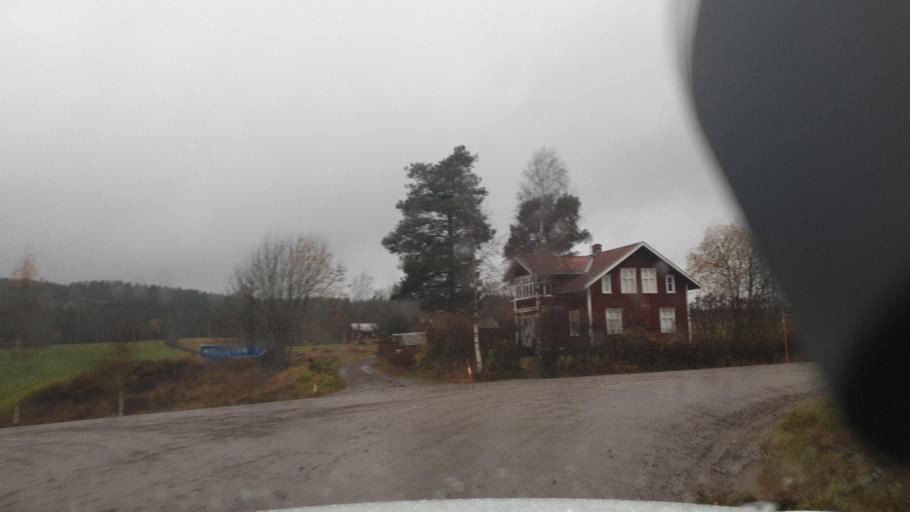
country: SE
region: Vaermland
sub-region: Eda Kommun
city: Amotfors
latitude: 59.7236
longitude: 12.1446
